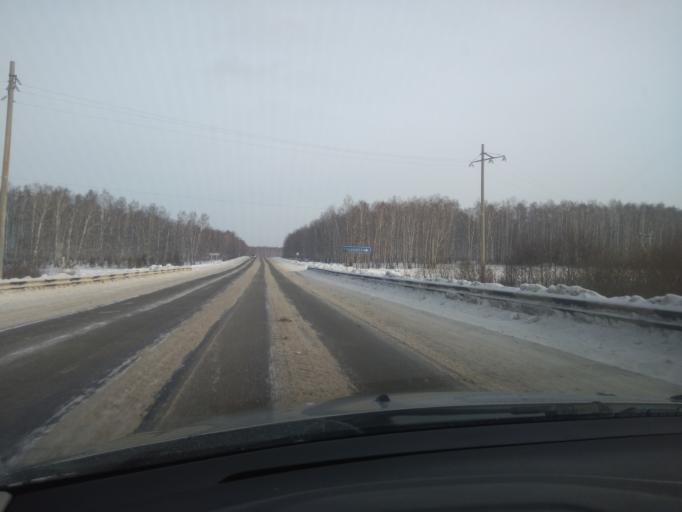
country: RU
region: Sverdlovsk
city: Bogdanovich
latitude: 56.7881
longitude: 61.9998
